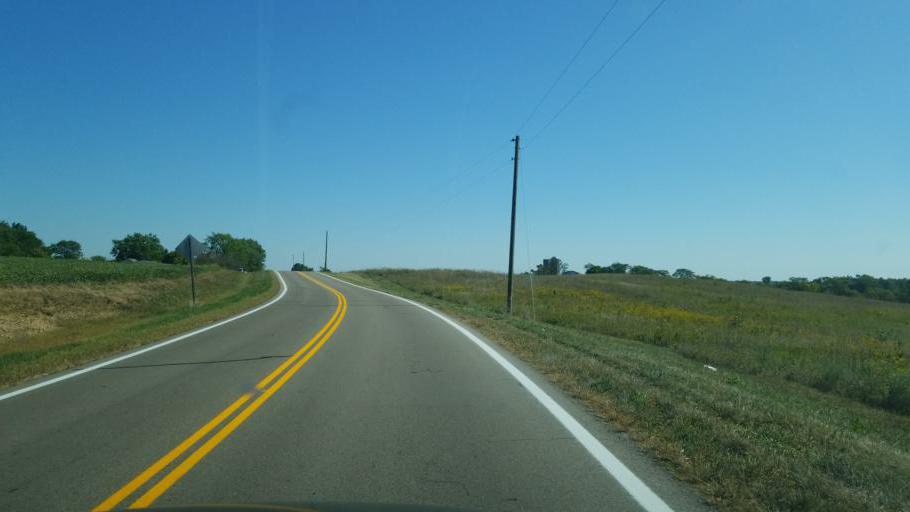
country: US
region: Ohio
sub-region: Champaign County
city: Mechanicsburg
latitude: 40.0955
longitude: -83.5793
